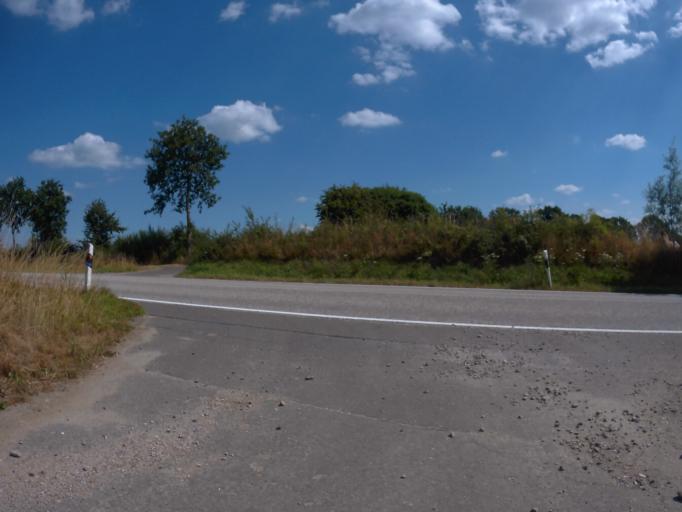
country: DE
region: Schleswig-Holstein
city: Suderstapel
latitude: 54.3594
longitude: 9.2233
